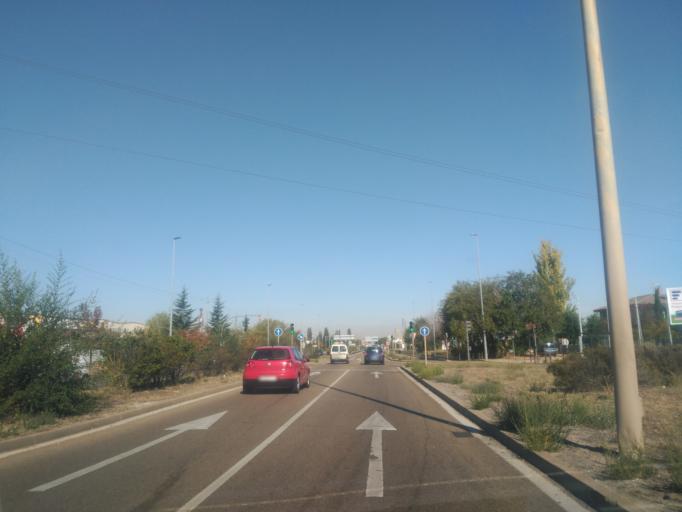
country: ES
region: Castille and Leon
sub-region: Provincia de Valladolid
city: Cisterniga
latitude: 41.6266
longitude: -4.6996
